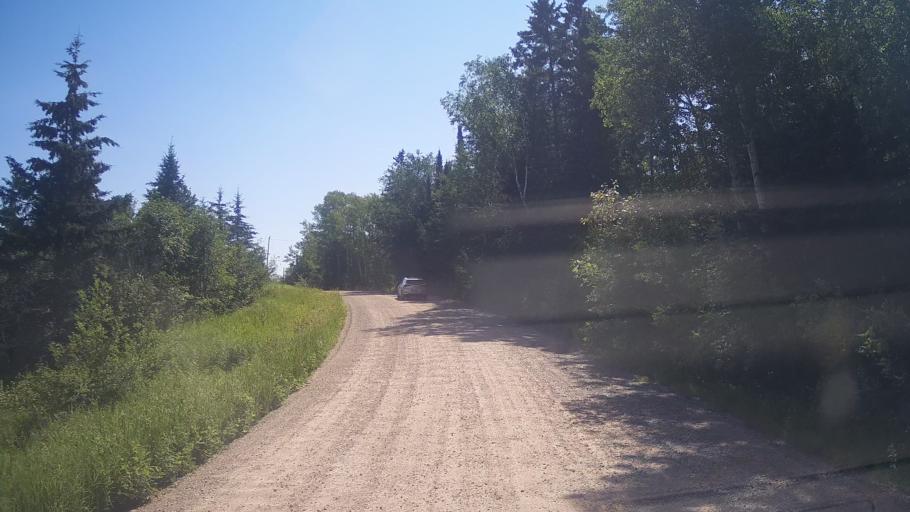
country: CA
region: Ontario
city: Dryden
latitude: 49.8154
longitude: -93.3257
